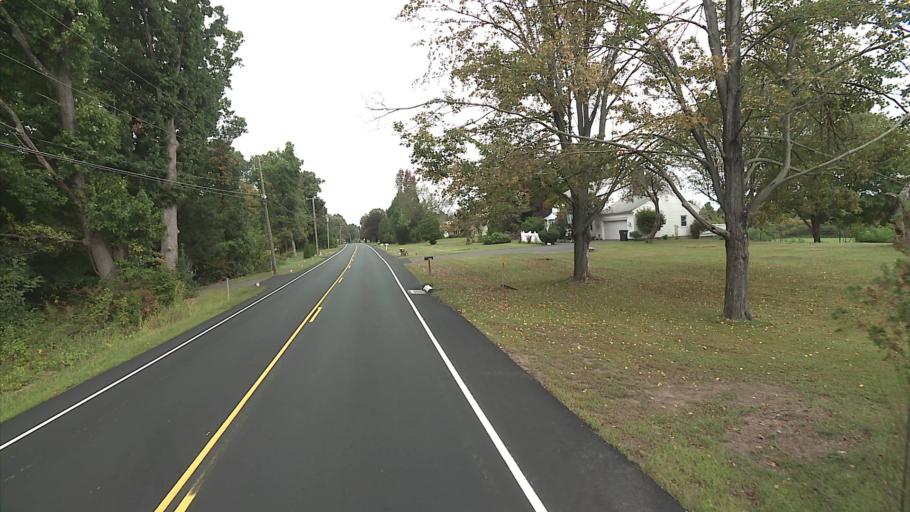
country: US
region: Connecticut
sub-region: Hartford County
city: Suffield Depot
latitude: 42.0051
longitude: -72.6945
